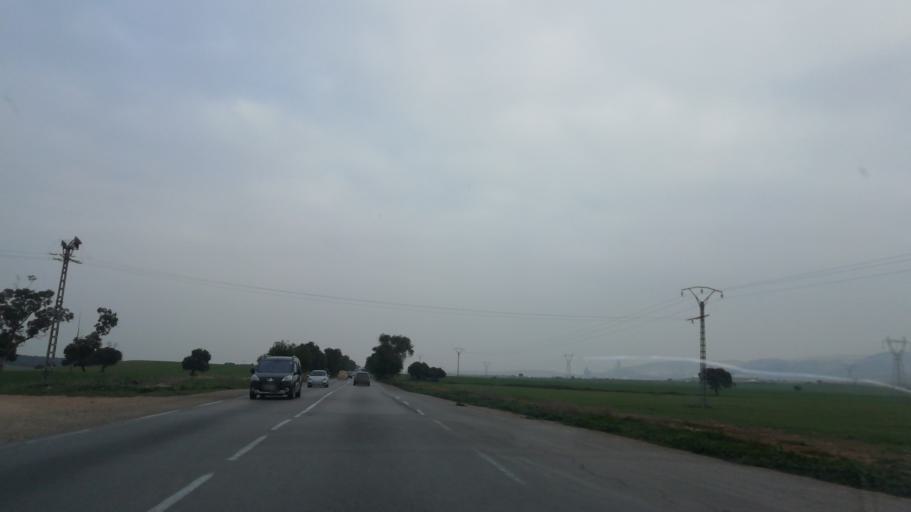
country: DZ
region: Mascara
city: Sig
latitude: 35.5393
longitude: -0.3353
